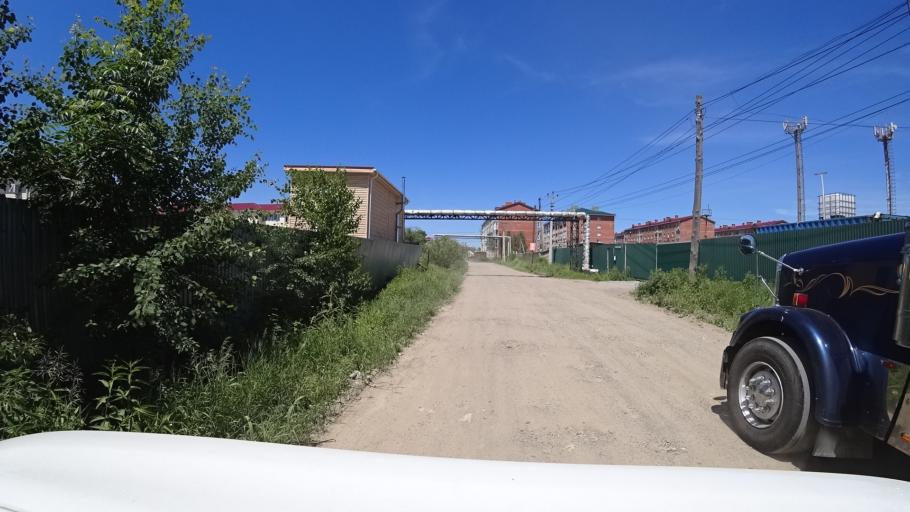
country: RU
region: Khabarovsk Krai
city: Topolevo
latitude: 48.5047
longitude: 135.1781
